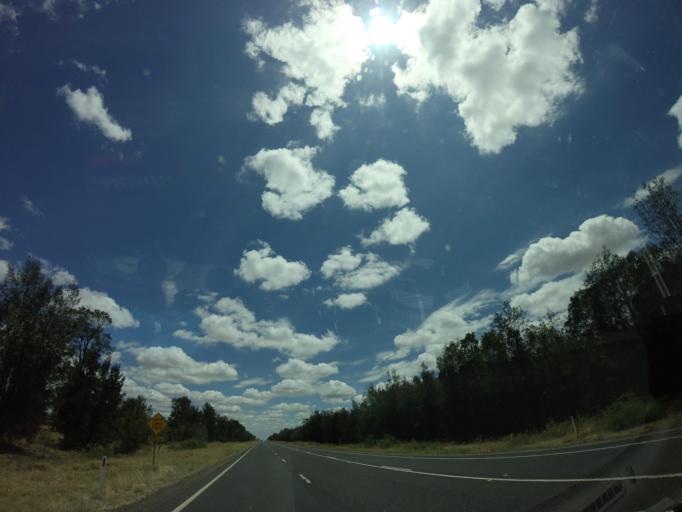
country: AU
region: New South Wales
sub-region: Moree Plains
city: Boggabilla
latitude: -28.9734
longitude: 150.0806
